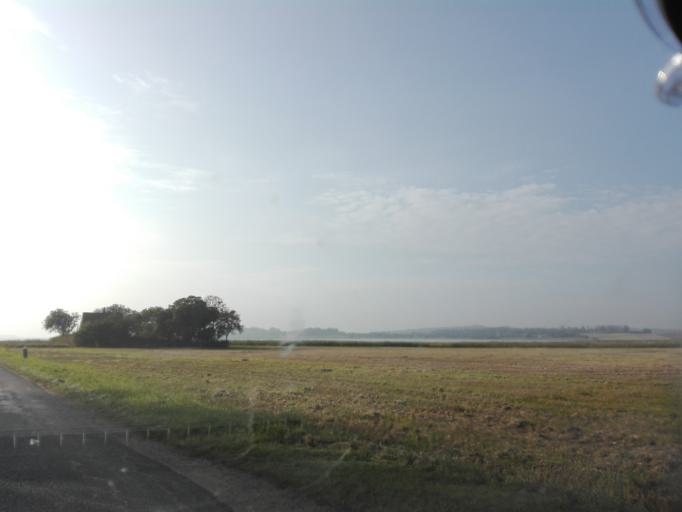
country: DK
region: Central Jutland
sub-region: Odder Kommune
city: Odder
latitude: 55.8739
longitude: 10.1490
